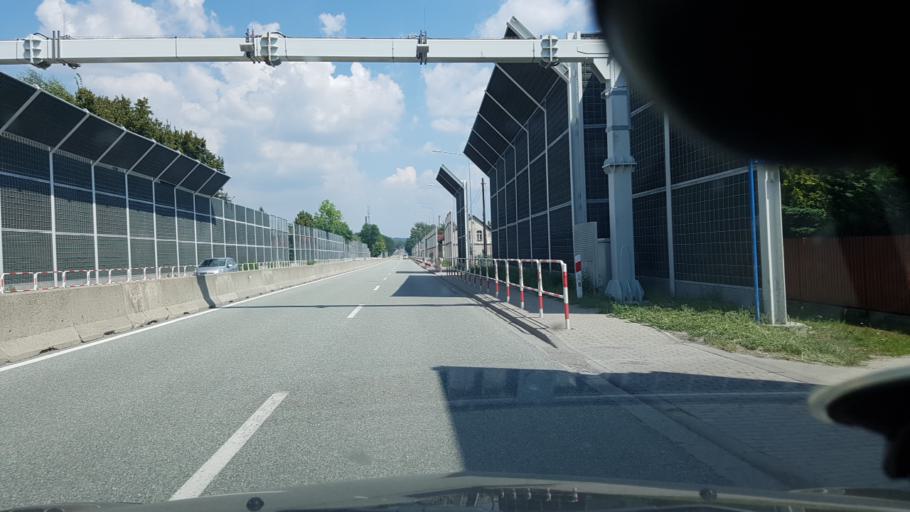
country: PL
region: Silesian Voivodeship
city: Gardawice
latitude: 50.1127
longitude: 18.7998
